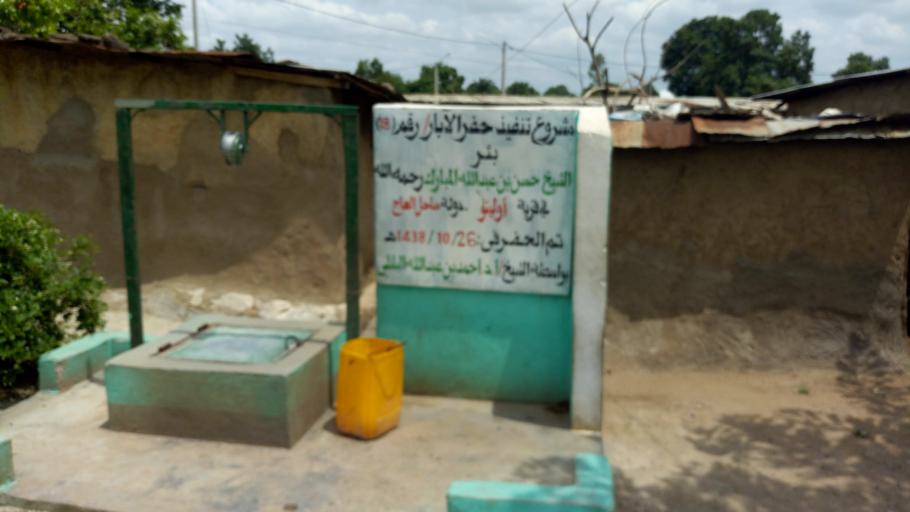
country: CI
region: Vallee du Bandama
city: Bouake
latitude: 7.6986
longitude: -4.9852
